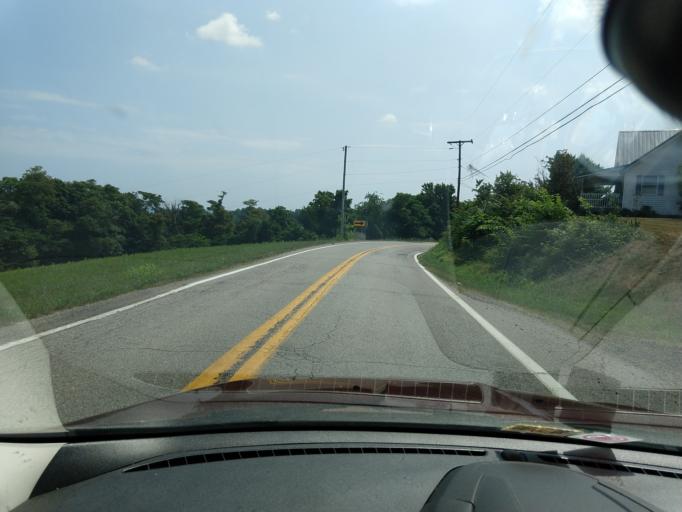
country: US
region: West Virginia
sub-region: Mason County
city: New Haven
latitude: 38.8654
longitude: -81.8952
